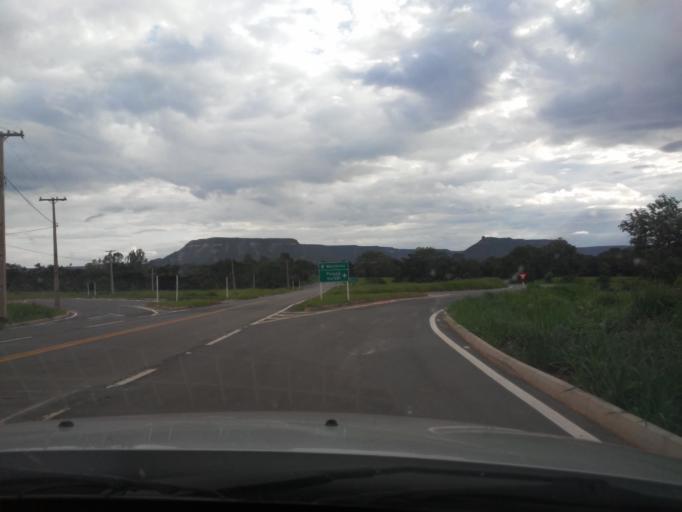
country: BR
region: Tocantins
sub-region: Taguatinga
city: Taguatinga
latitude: -12.3891
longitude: -46.4136
